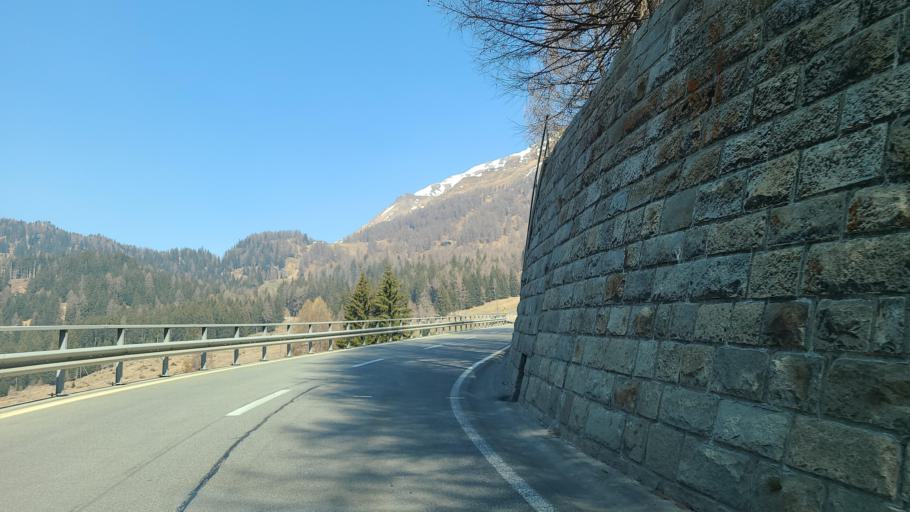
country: CH
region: Grisons
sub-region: Bernina District
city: Poschiavo
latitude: 46.3858
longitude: 10.0798
